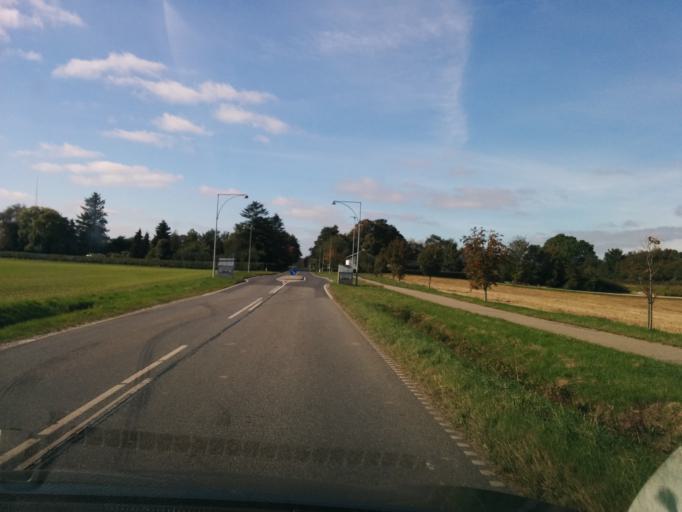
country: DK
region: South Denmark
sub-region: Kolding Kommune
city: Sonder Bjert
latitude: 55.4049
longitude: 9.5403
